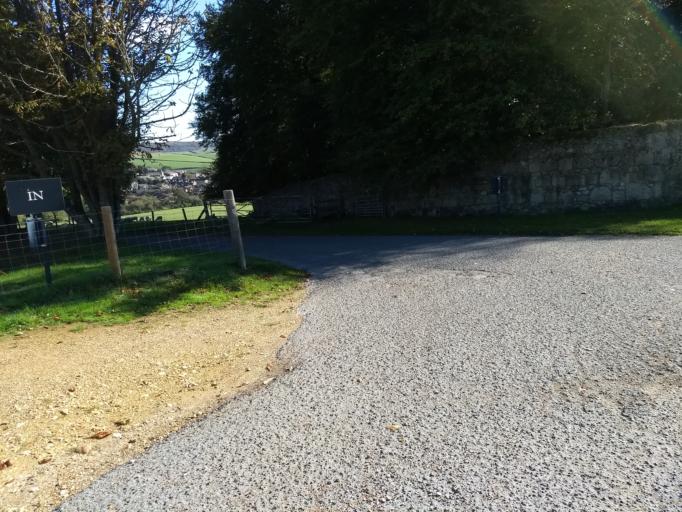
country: GB
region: England
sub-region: Isle of Wight
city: Ventnor
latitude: 50.6183
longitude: -1.2340
